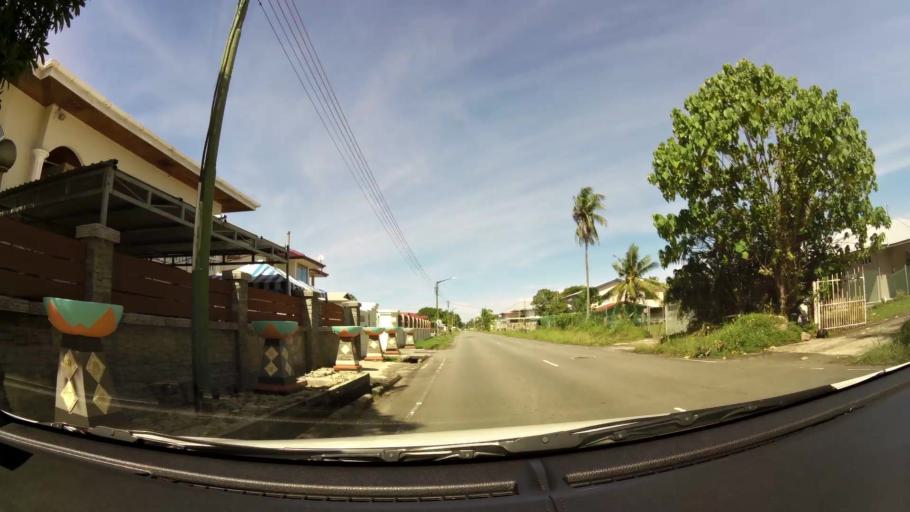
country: BN
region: Belait
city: Kuala Belait
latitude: 4.5872
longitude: 114.2150
